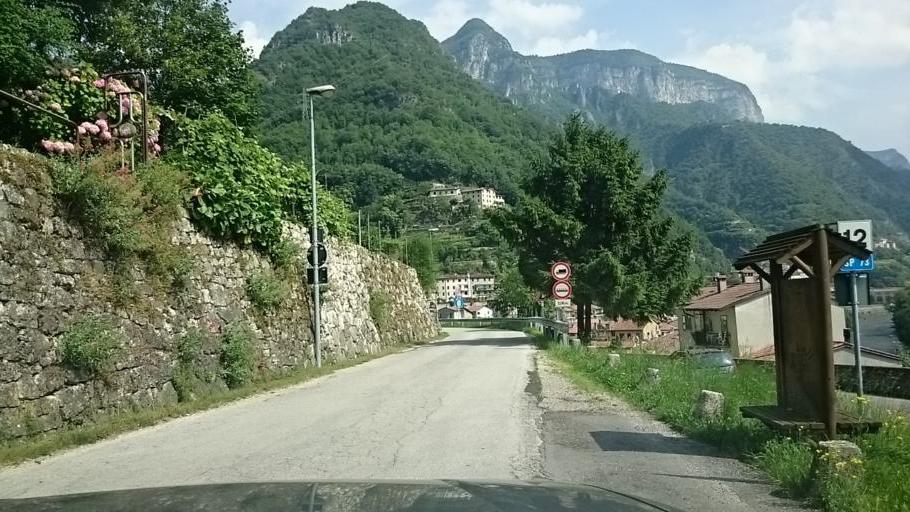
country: IT
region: Veneto
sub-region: Provincia di Vicenza
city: Valstagna
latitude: 45.8585
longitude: 11.6579
